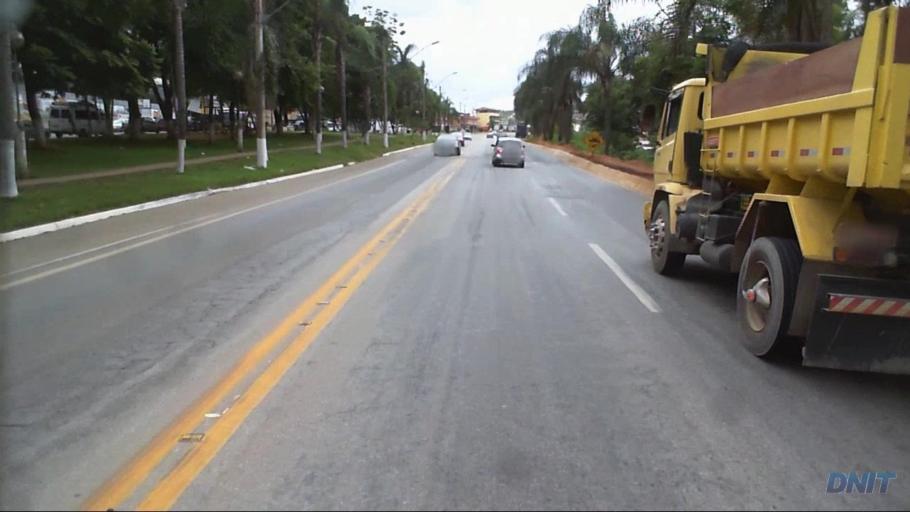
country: BR
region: Minas Gerais
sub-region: Joao Monlevade
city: Joao Monlevade
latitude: -19.8388
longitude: -43.1829
